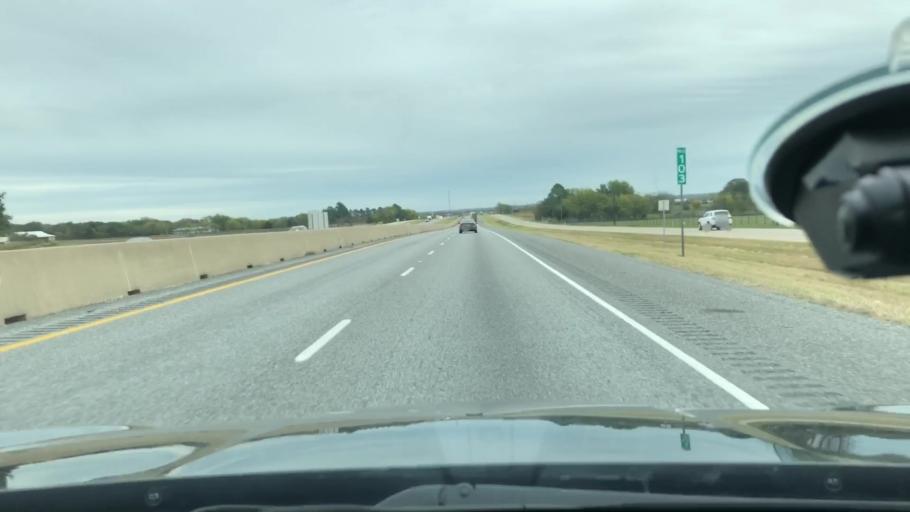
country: US
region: Texas
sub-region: Hunt County
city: Commerce
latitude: 33.1296
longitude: -95.9662
